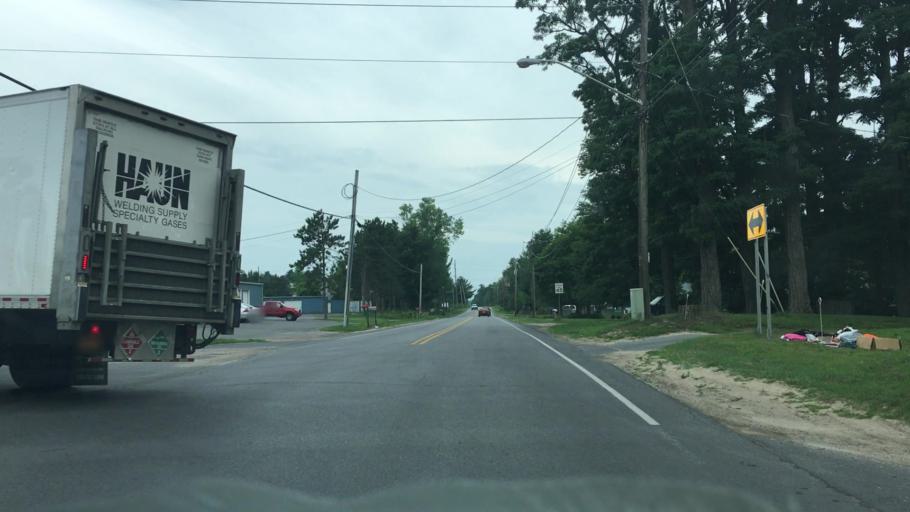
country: US
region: New York
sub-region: Clinton County
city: Plattsburgh West
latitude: 44.6662
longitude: -73.5078
